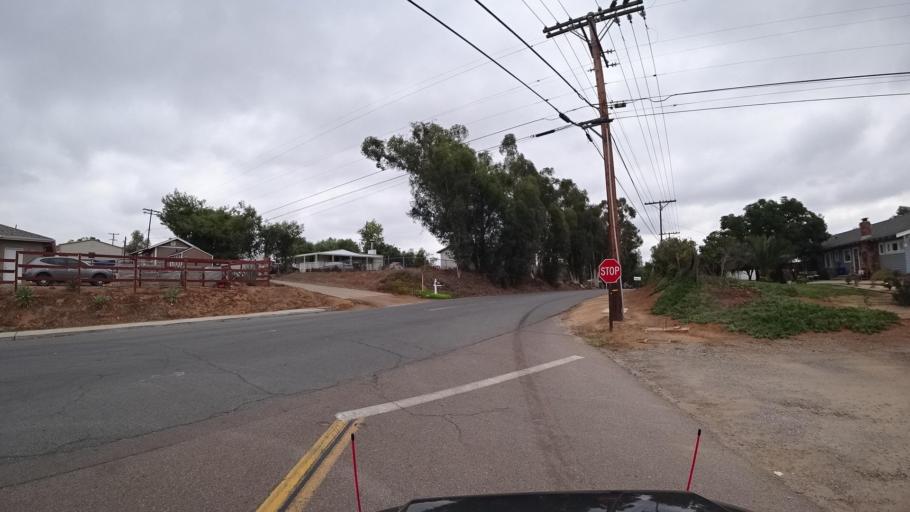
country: US
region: California
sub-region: San Diego County
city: Ramona
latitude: 33.0313
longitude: -116.8580
